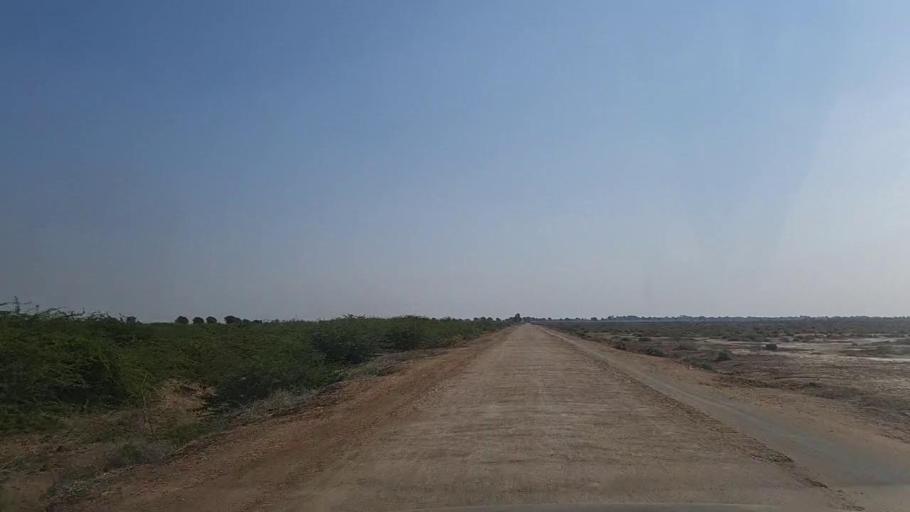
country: PK
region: Sindh
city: Digri
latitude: 25.1653
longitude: 69.1697
